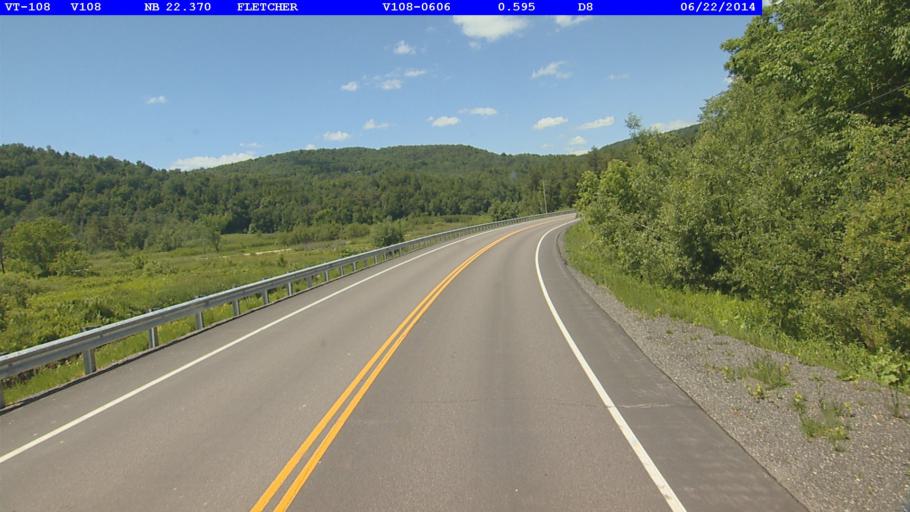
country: US
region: Vermont
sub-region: Lamoille County
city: Johnson
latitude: 44.7106
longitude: -72.8379
